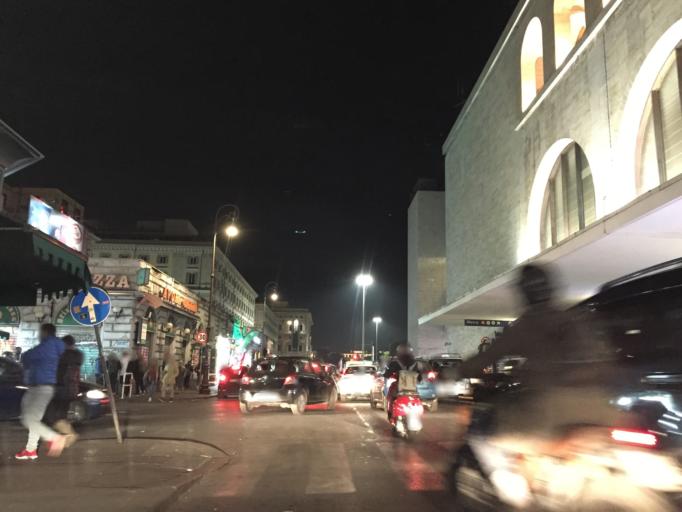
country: IT
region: Latium
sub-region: Citta metropolitana di Roma Capitale
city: Rome
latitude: 41.8997
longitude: 12.5016
